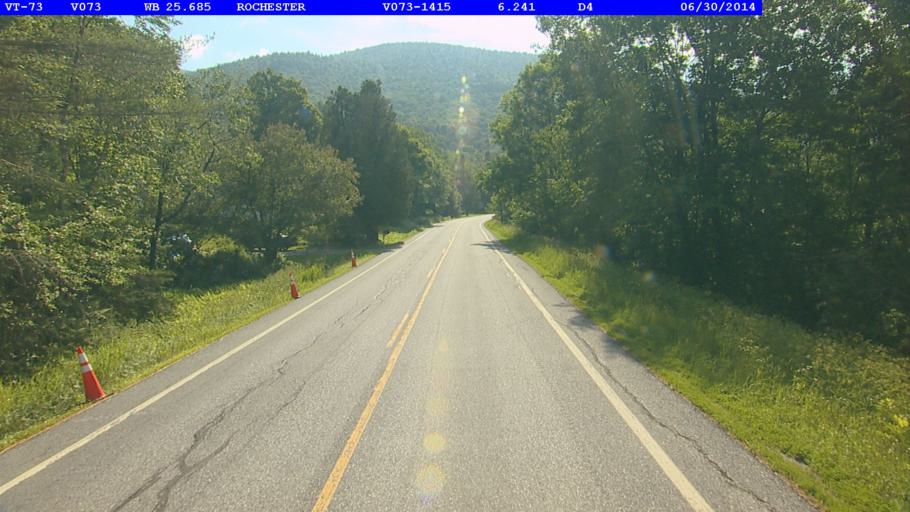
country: US
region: Vermont
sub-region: Orange County
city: Randolph
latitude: 43.8482
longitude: -72.8519
